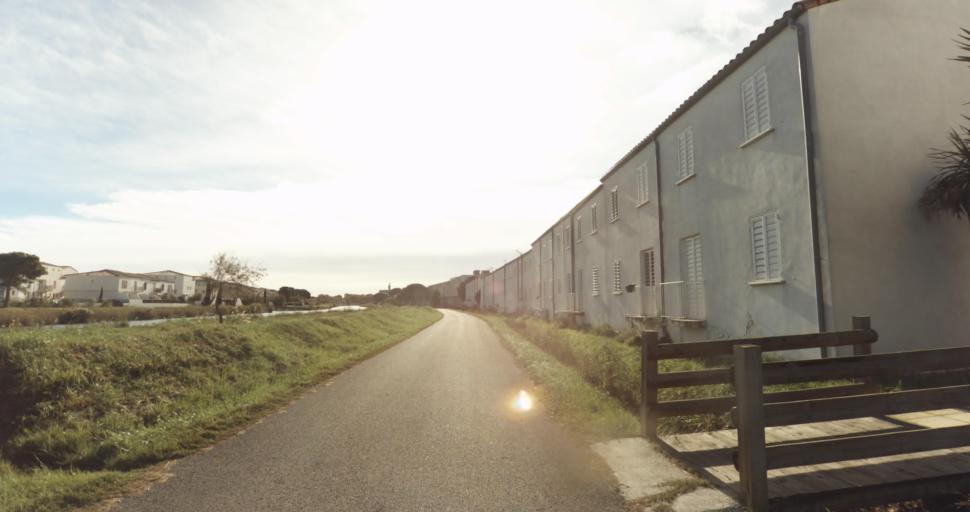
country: FR
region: Languedoc-Roussillon
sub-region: Departement du Gard
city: Aigues-Mortes
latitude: 43.5754
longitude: 4.1838
